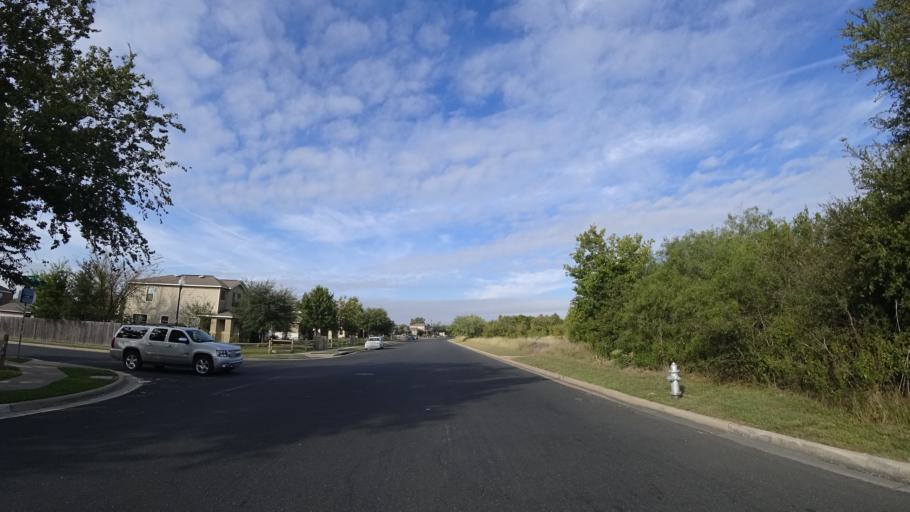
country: US
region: Texas
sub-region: Travis County
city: Austin
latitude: 30.2005
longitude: -97.7320
